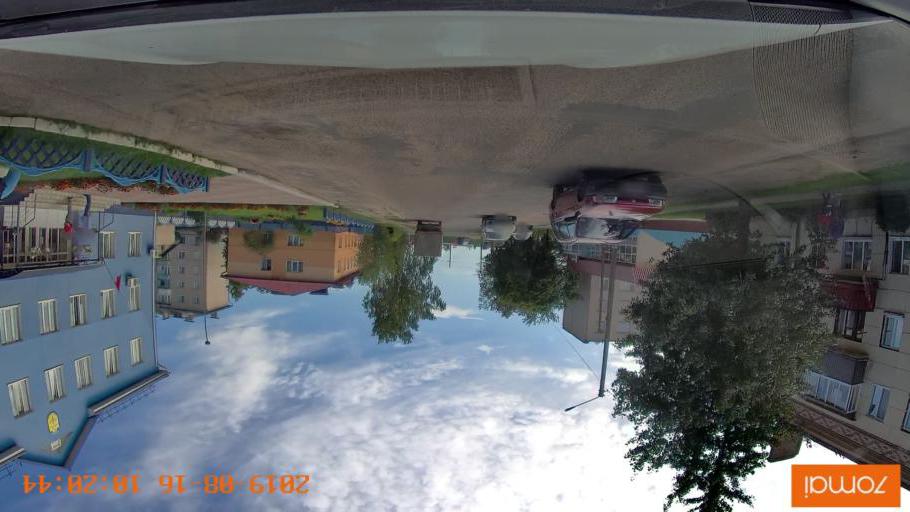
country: BY
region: Mogilev
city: Asipovichy
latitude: 53.2983
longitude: 28.6606
